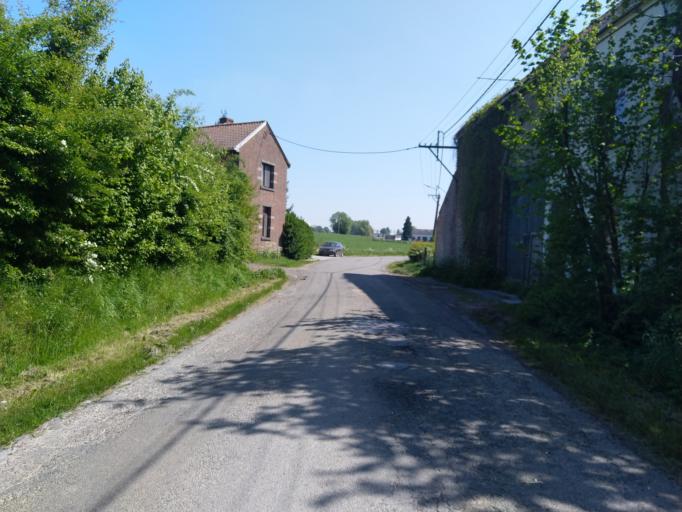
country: BE
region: Wallonia
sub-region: Province du Brabant Wallon
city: Rebecq-Rognon
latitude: 50.6104
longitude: 4.1028
